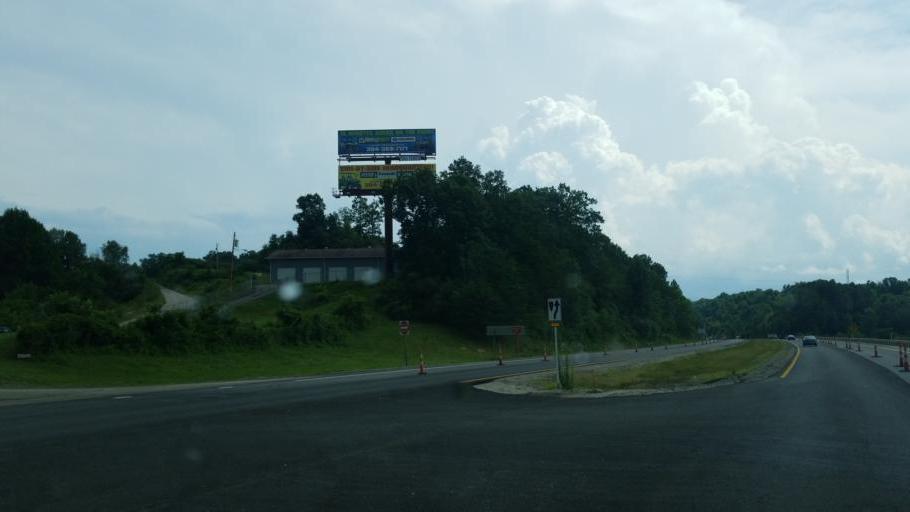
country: US
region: West Virginia
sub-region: Kanawha County
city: Alum Creek
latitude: 38.2397
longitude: -81.8391
